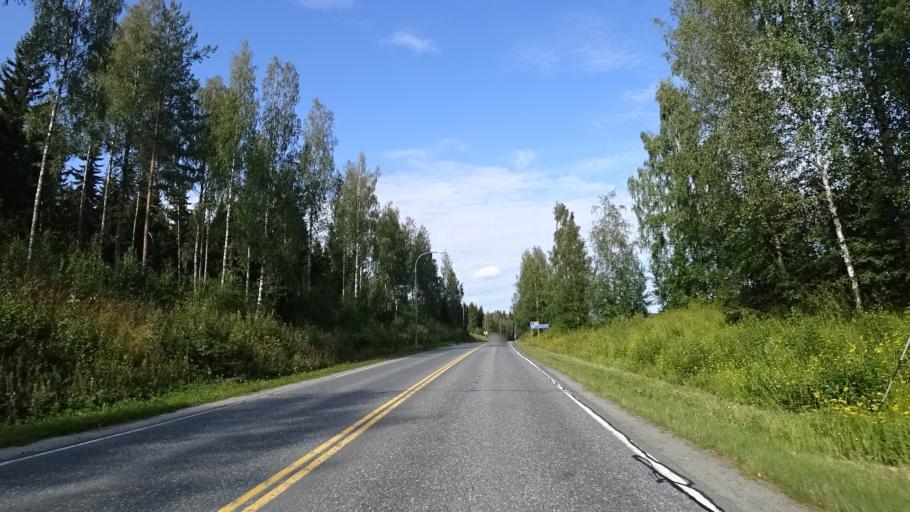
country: FI
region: North Karelia
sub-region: Joensuu
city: Eno
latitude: 62.7884
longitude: 30.0812
